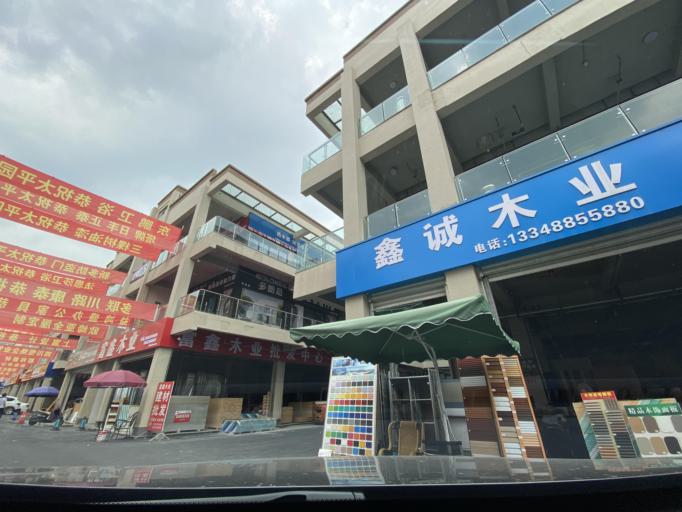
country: CN
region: Sichuan
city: Dongsheng
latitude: 30.6087
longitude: 103.9416
